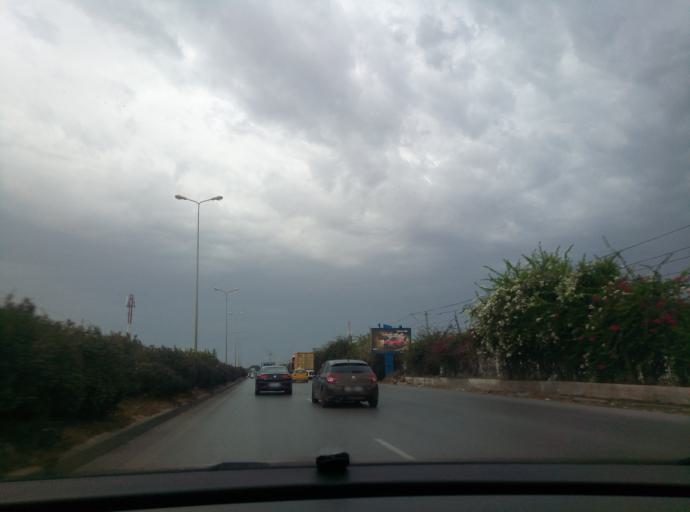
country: TN
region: Bin 'Arus
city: Ben Arous
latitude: 36.7532
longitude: 10.2035
